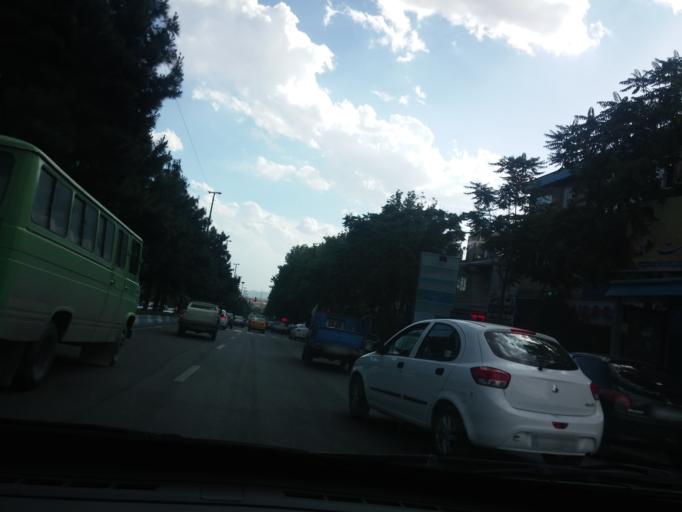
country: IR
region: Tehran
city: Damavand
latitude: 35.7347
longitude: 51.9082
